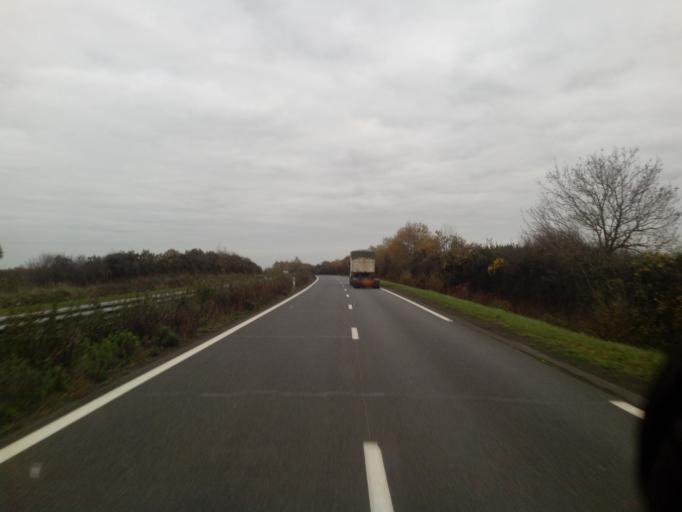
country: FR
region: Pays de la Loire
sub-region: Departement de la Loire-Atlantique
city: Vallet
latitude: 47.1546
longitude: -1.2251
